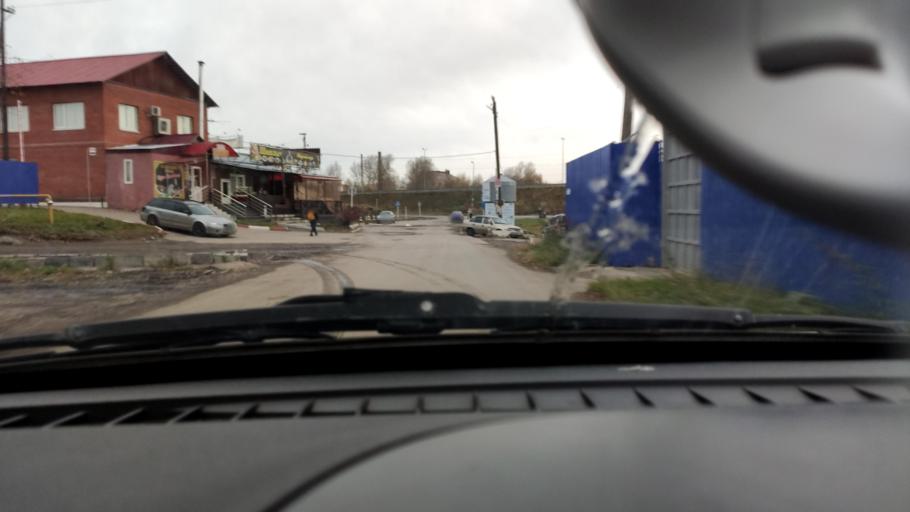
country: RU
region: Perm
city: Kondratovo
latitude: 57.9990
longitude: 56.1233
